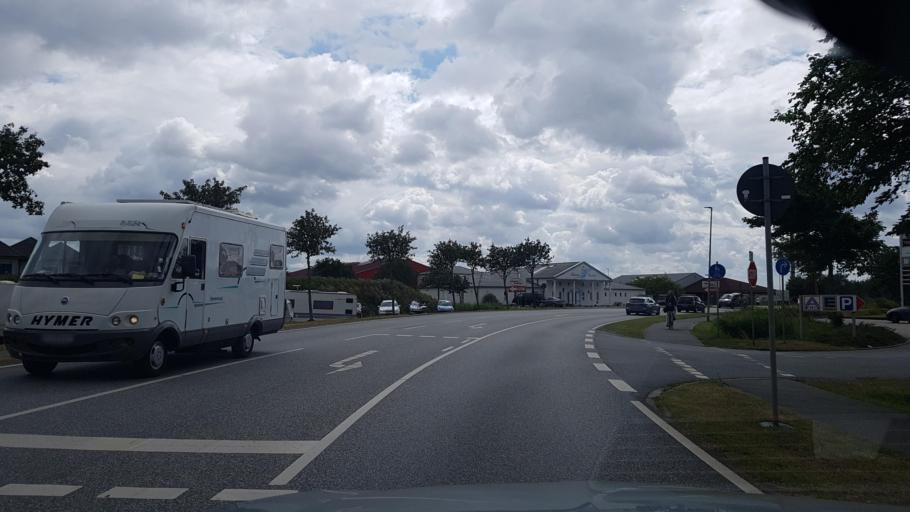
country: DE
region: Schleswig-Holstein
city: Busumer Deichhausen
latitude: 54.1390
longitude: 8.8744
